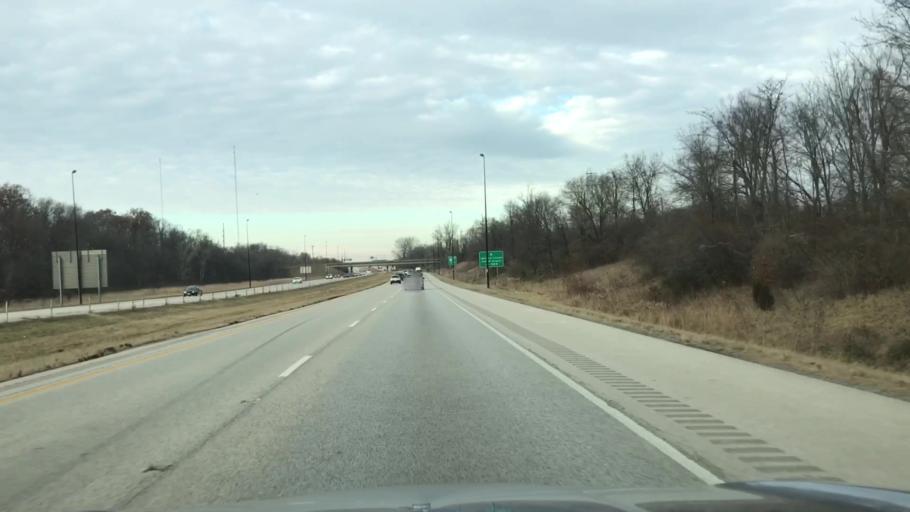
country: US
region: Illinois
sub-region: Sangamon County
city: Grandview
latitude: 39.8196
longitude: -89.5926
